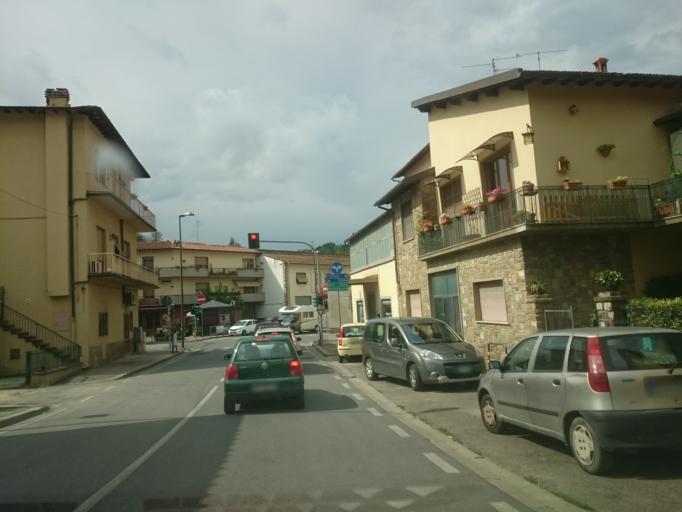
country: IT
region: Tuscany
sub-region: Province of Florence
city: Greve in Chianti
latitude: 43.5864
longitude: 11.3157
